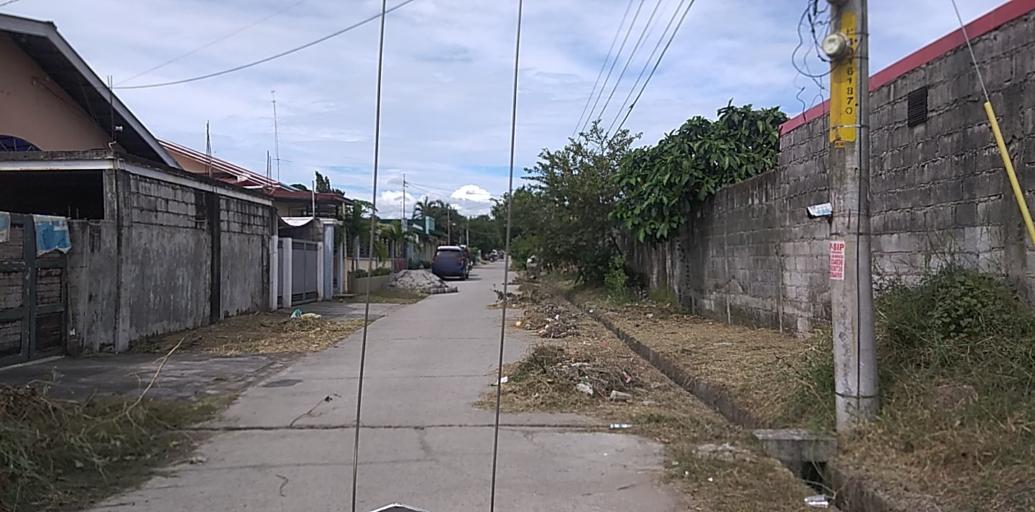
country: PH
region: Central Luzon
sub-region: Province of Pampanga
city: Manibaug Pasig
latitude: 15.1124
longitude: 120.5604
